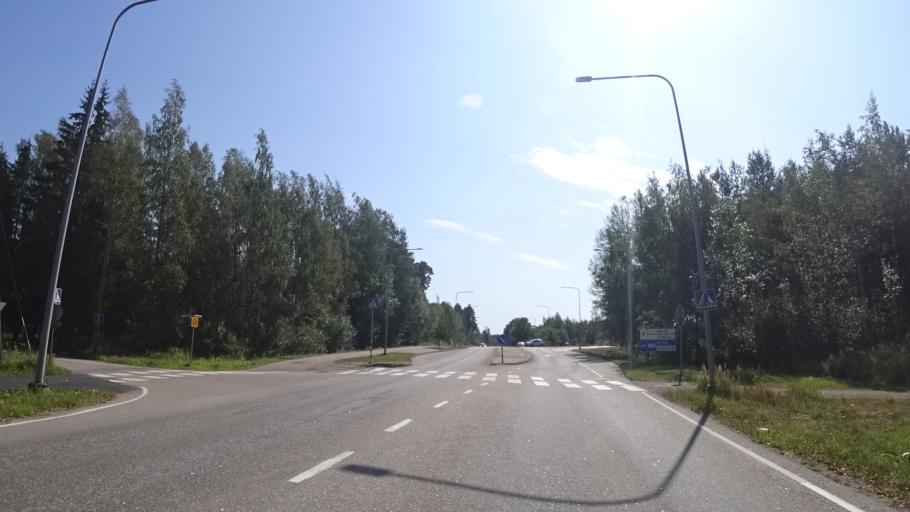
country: FI
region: Kymenlaakso
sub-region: Kotka-Hamina
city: Karhula
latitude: 60.5181
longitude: 26.9550
